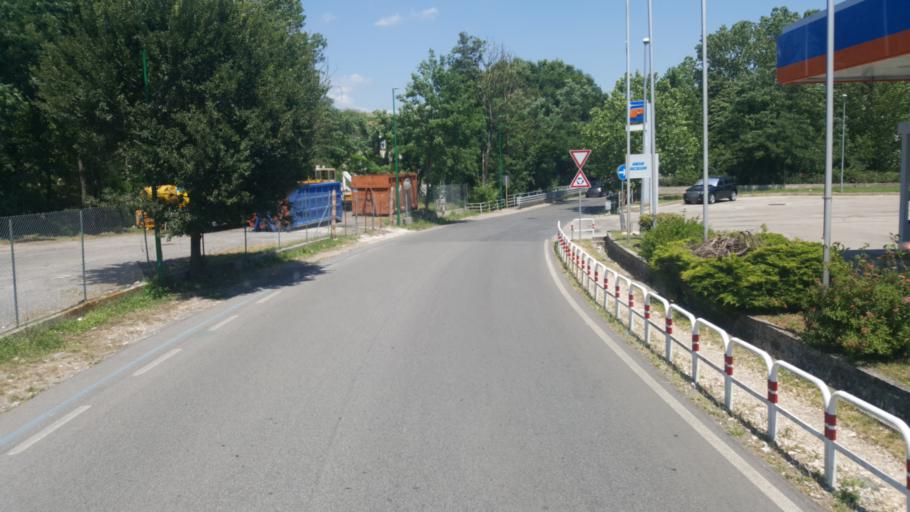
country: IT
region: Latium
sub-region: Citta metropolitana di Roma Capitale
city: Colleferro
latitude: 41.7415
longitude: 13.0020
